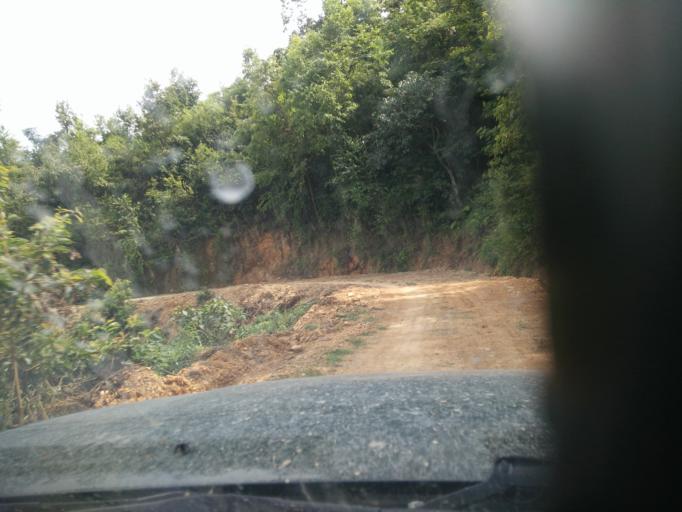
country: CN
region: Guangxi Zhuangzu Zizhiqu
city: Leli
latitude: 24.7687
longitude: 105.9039
